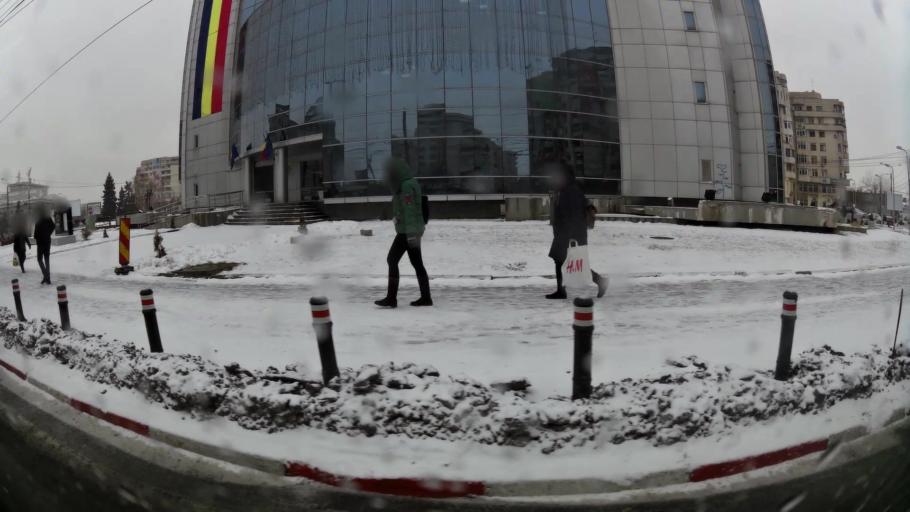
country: RO
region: Prahova
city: Ploiesti
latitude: 44.9426
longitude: 26.0182
